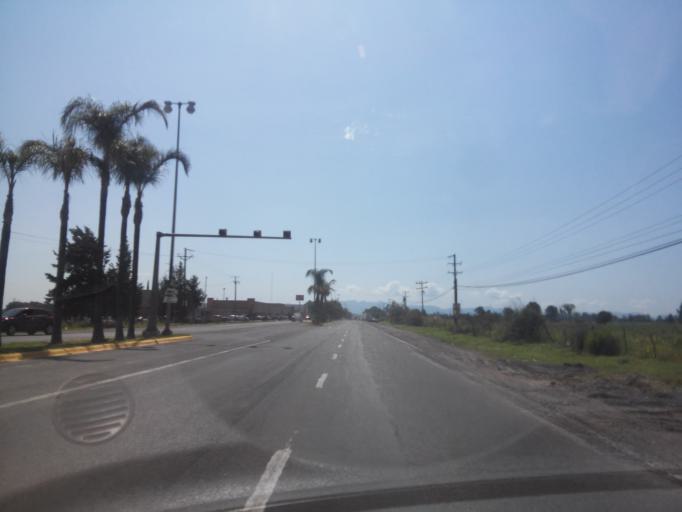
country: MX
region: Durango
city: Victoria de Durango
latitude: 23.9939
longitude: -104.6313
